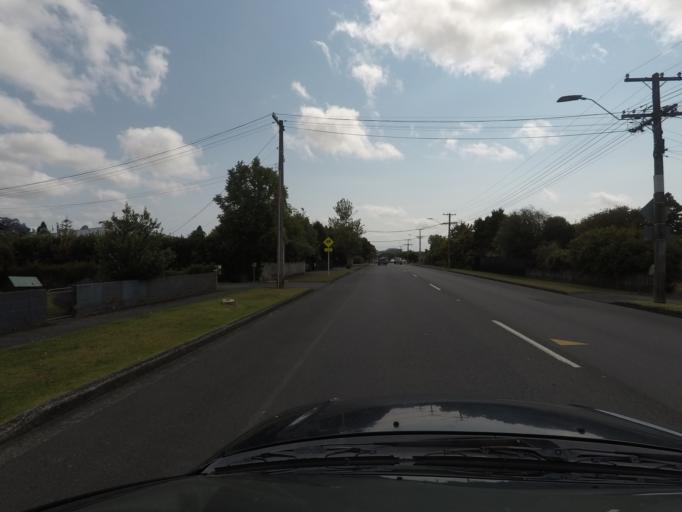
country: NZ
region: Northland
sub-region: Whangarei
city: Whangarei
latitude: -35.6877
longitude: 174.3243
